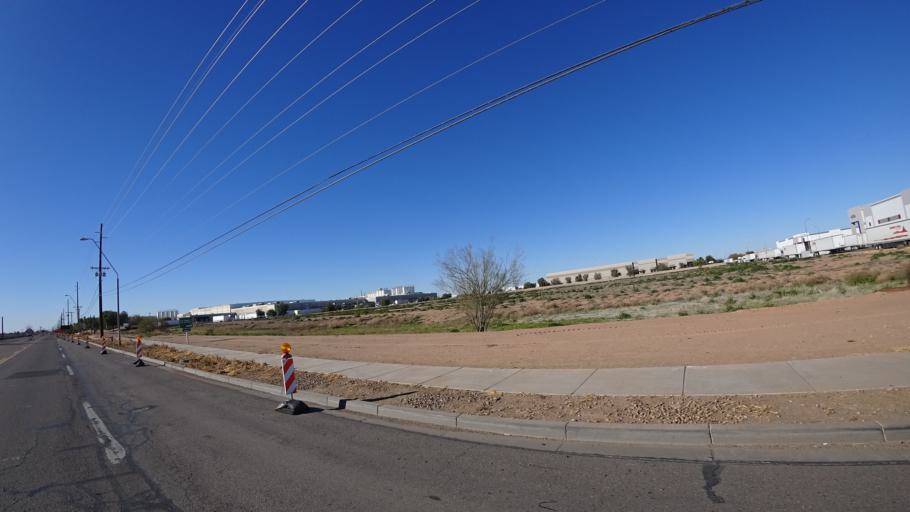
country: US
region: Arizona
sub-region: Maricopa County
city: Tolleson
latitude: 33.4358
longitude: -112.2619
